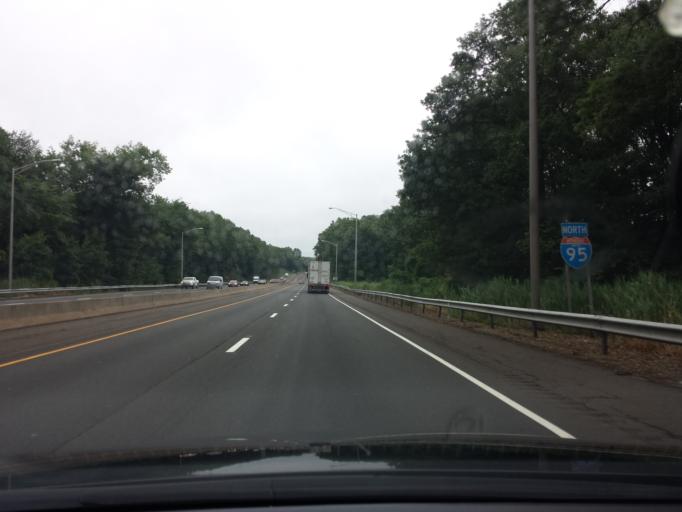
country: US
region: Connecticut
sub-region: New Haven County
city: Branford
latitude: 41.2894
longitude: -72.8143
